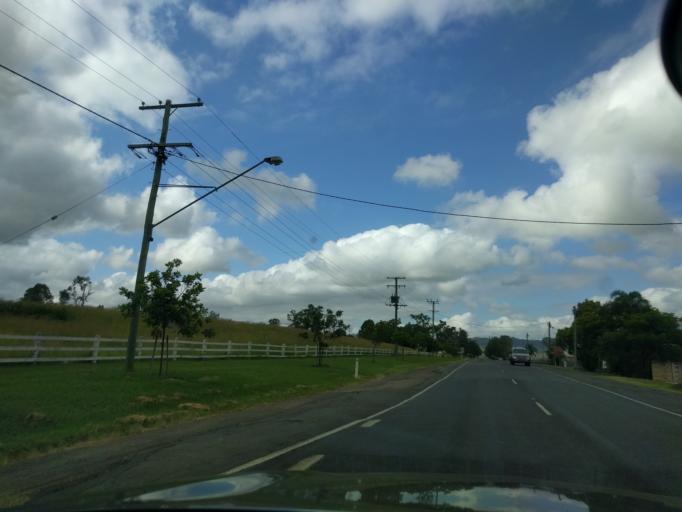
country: AU
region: Queensland
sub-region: Logan
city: Cedar Vale
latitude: -27.9976
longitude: 152.9885
